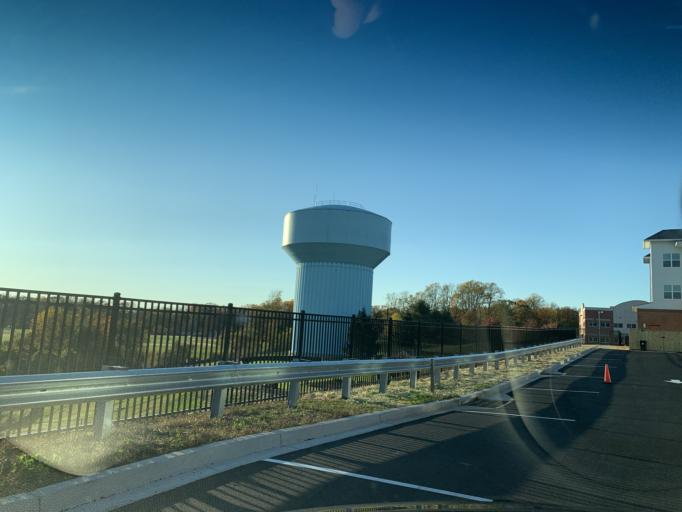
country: US
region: Maryland
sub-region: Harford County
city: Bel Air North
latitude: 39.5711
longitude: -76.3843
